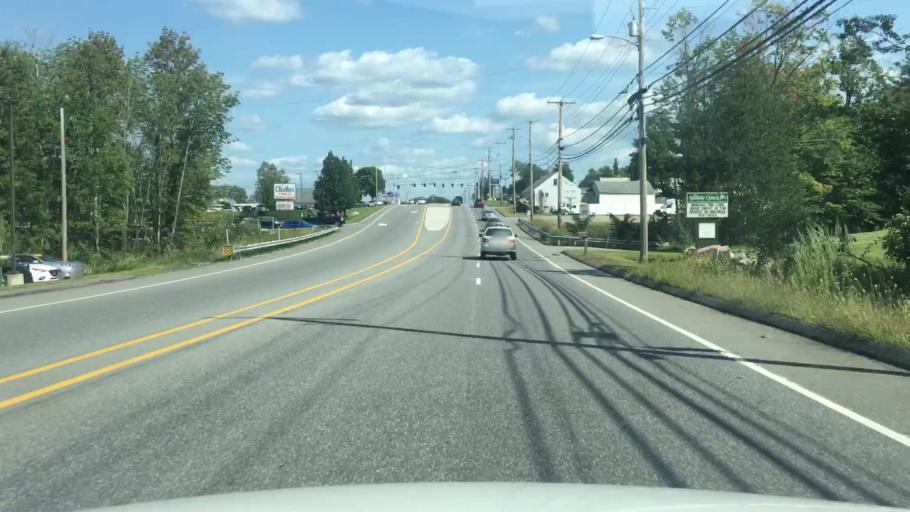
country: US
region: Maine
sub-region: Kennebec County
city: Manchester
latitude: 44.3205
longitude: -69.8266
